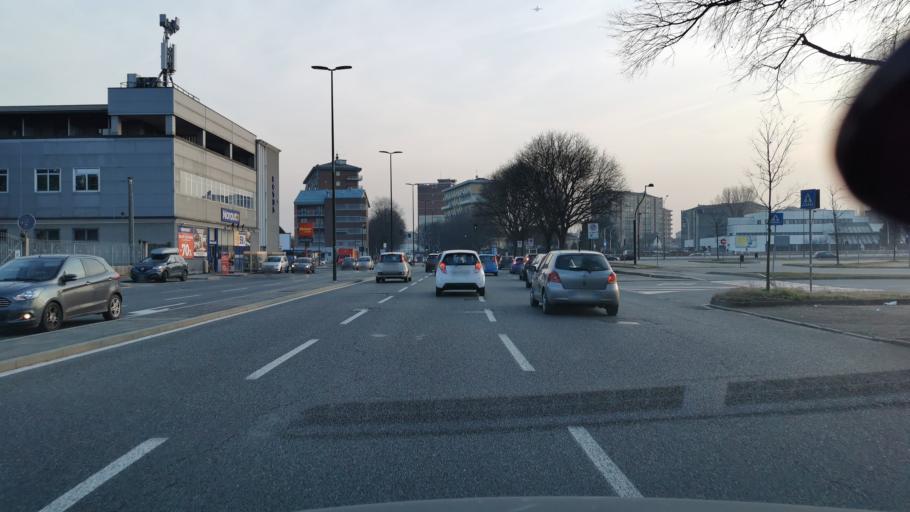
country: IT
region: Piedmont
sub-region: Provincia di Torino
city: Venaria Reale
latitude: 45.1078
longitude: 7.6451
